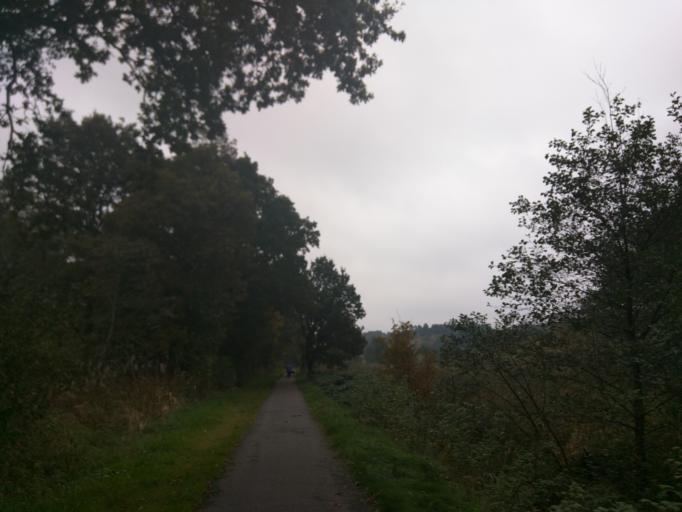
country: DK
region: Central Jutland
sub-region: Silkeborg Kommune
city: Silkeborg
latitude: 56.2339
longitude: 9.5231
